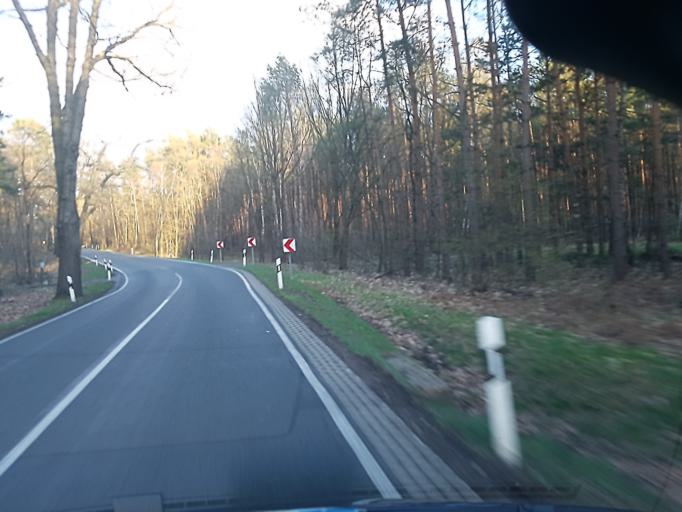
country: DE
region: Saxony
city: Trossin
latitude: 51.5655
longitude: 12.7771
